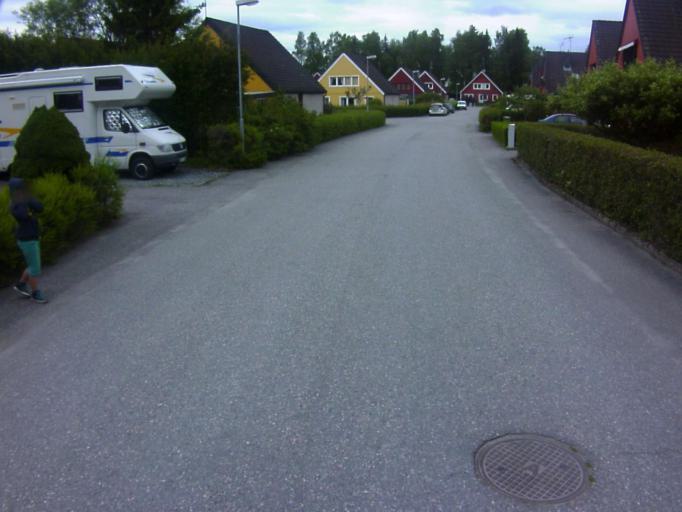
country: SE
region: Soedermanland
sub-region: Eskilstuna Kommun
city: Skogstorp
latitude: 59.3184
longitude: 16.4818
